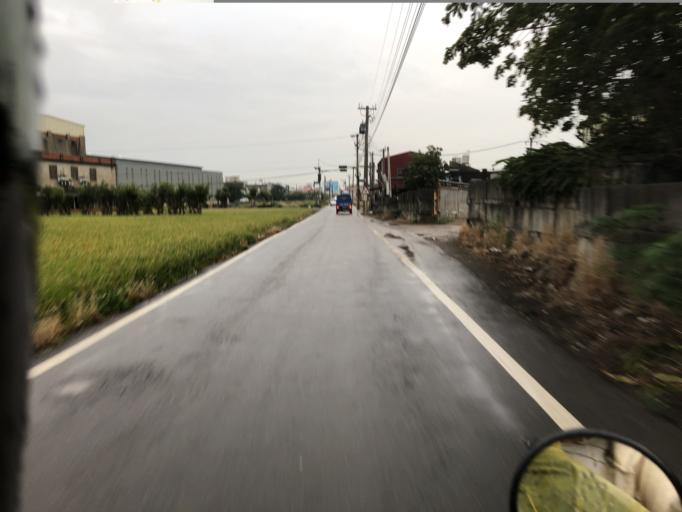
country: TW
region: Taiwan
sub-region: Hsinchu
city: Zhubei
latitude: 24.8449
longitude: 120.9869
